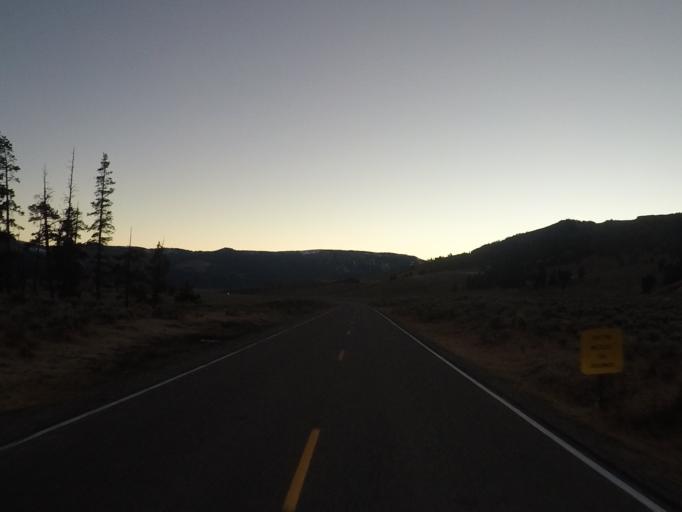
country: US
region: Montana
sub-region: Park County
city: Livingston
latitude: 44.8940
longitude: -110.1309
